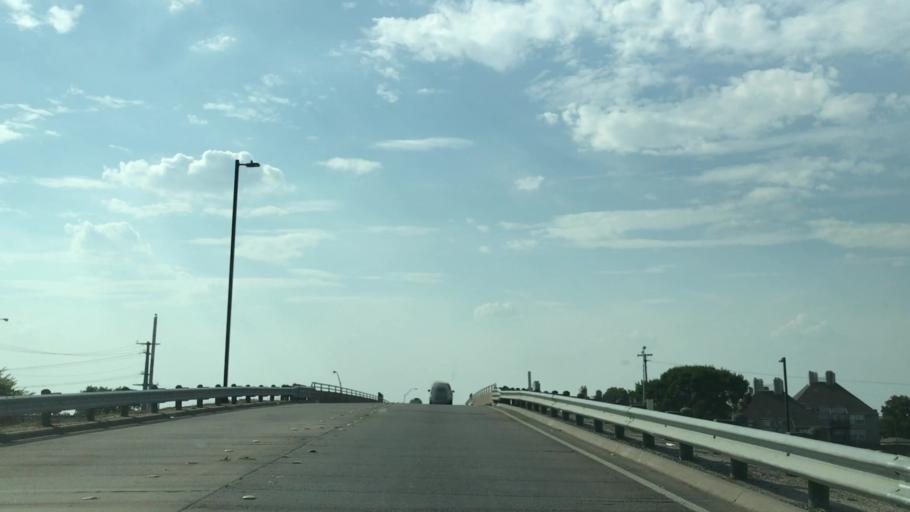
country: US
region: Texas
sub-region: Dallas County
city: Rowlett
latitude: 32.8641
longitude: -96.5432
